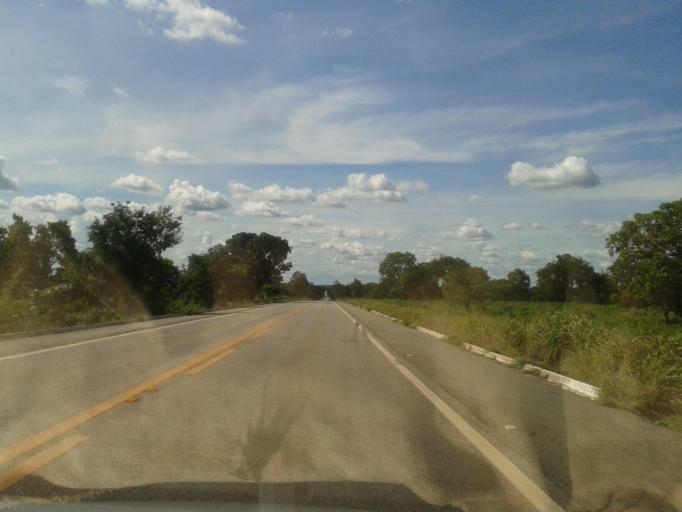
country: BR
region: Goias
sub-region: Mozarlandia
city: Mozarlandia
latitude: -15.2444
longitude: -50.5083
